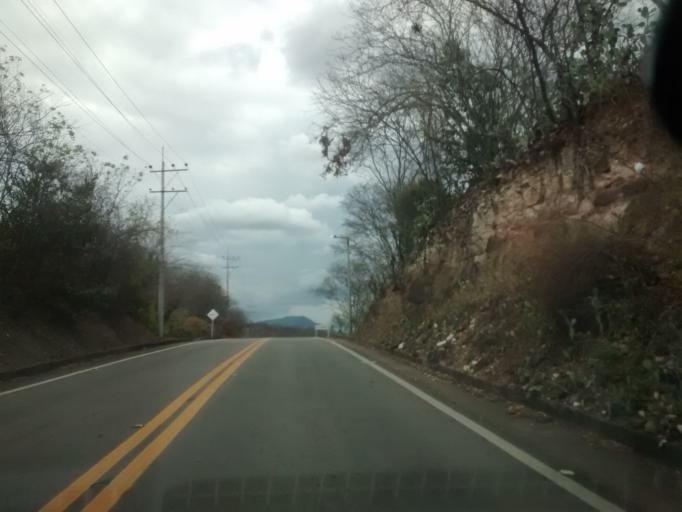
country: CO
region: Cundinamarca
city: Agua de Dios
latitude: 4.4322
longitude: -74.6889
